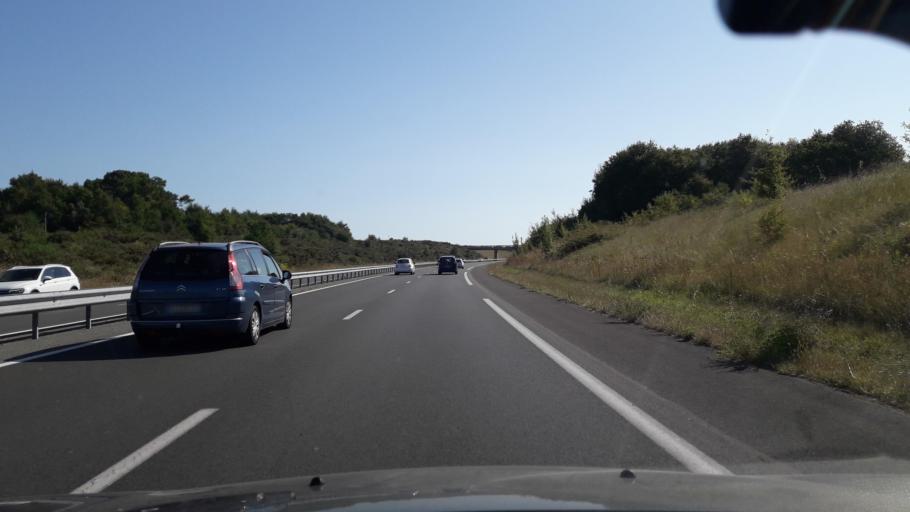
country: FR
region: Poitou-Charentes
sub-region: Departement de la Charente-Maritime
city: Saint-Romain-de-Benet
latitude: 45.6872
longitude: -0.8699
